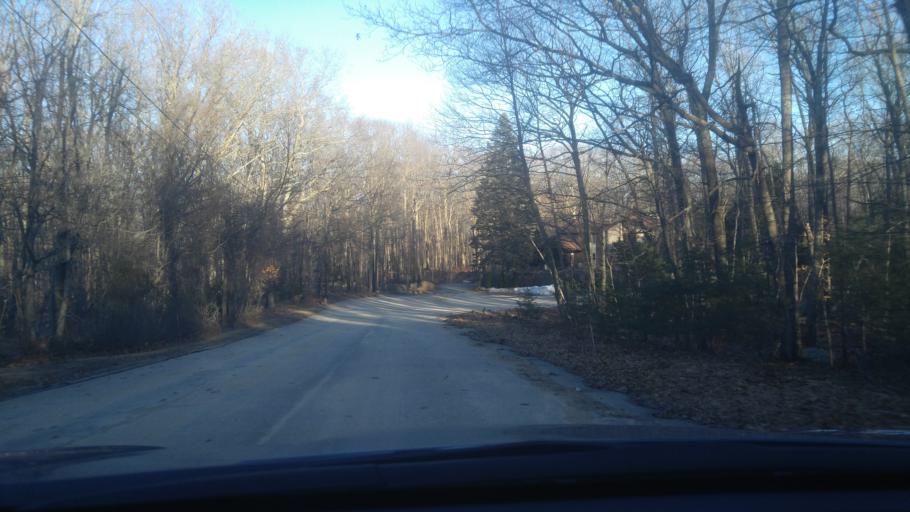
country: US
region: Rhode Island
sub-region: Kent County
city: West Warwick
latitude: 41.6495
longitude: -71.5481
